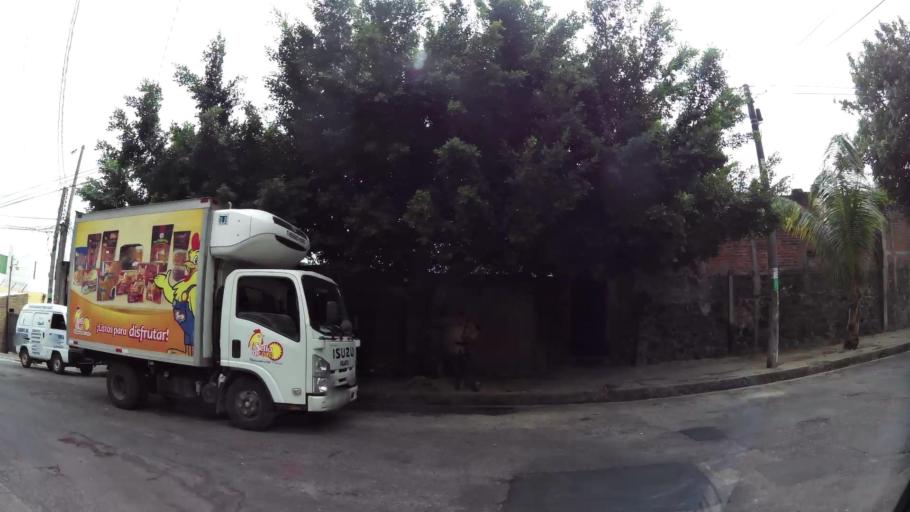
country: SV
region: La Libertad
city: Santa Tecla
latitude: 13.7106
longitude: -89.2571
